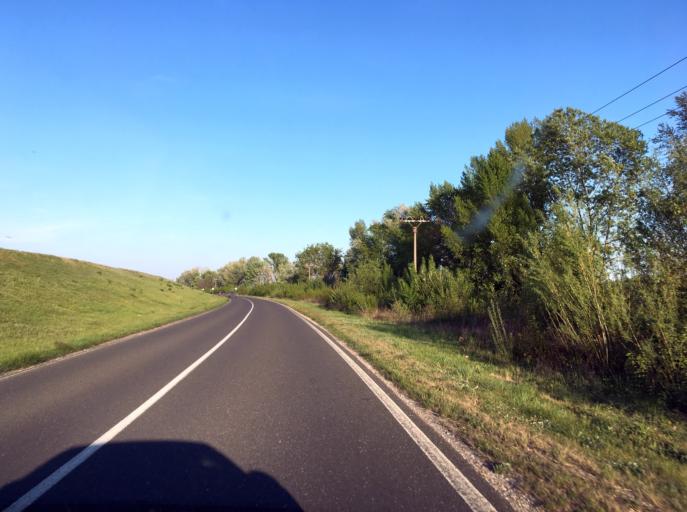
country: SK
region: Trnavsky
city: Samorin
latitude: 47.9967
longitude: 17.2731
